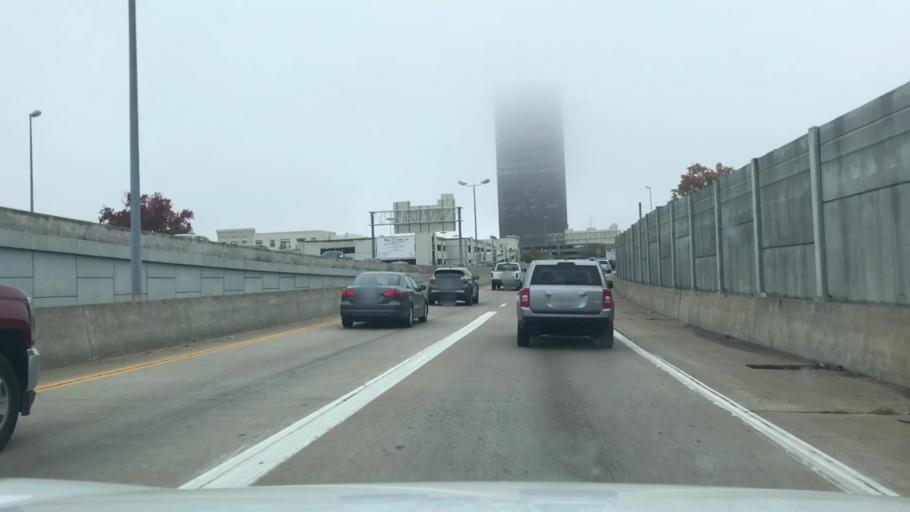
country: US
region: Missouri
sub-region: Saint Louis County
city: Brentwood
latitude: 38.6322
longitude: -90.3442
